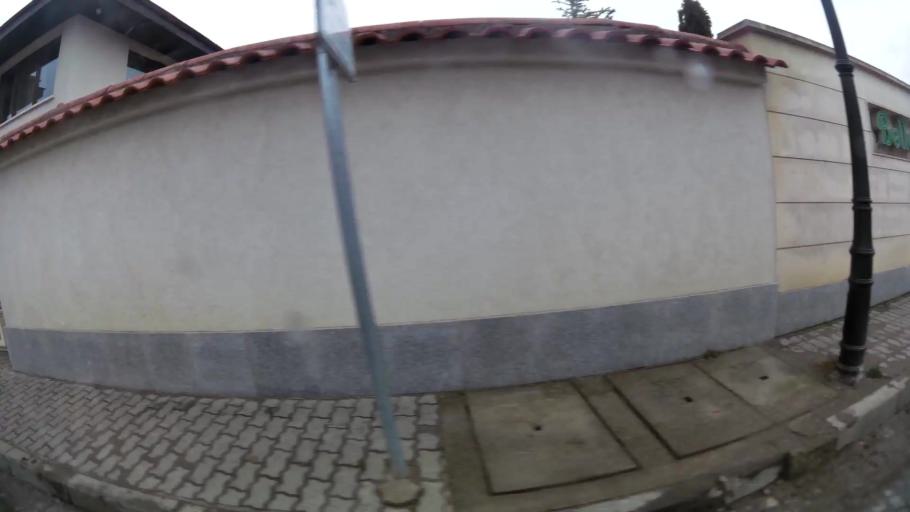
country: BG
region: Sofia-Capital
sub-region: Stolichna Obshtina
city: Sofia
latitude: 42.6150
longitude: 23.3761
